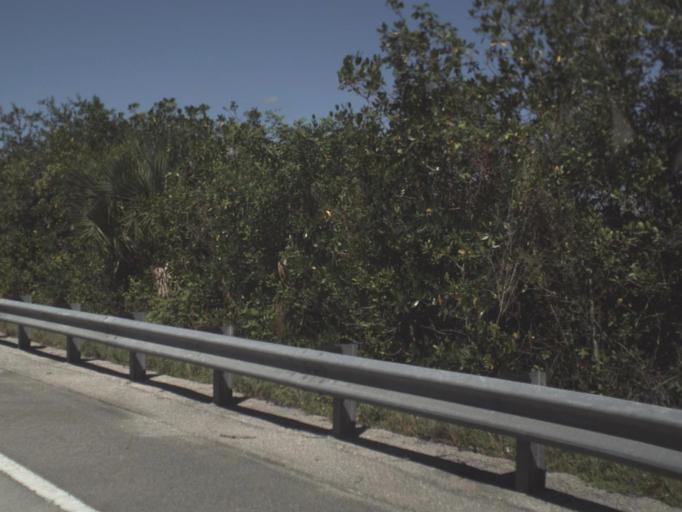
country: US
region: Florida
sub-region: Collier County
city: Marco
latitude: 25.9707
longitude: -81.5440
